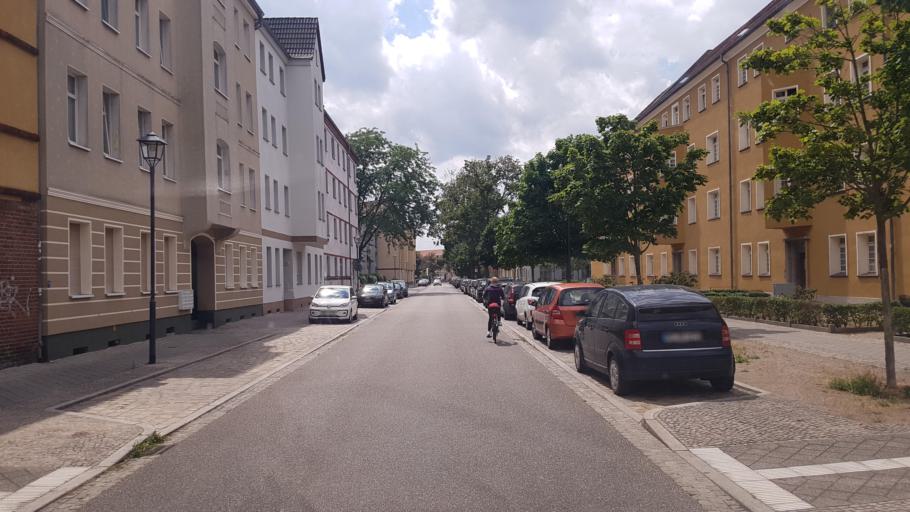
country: DE
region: Brandenburg
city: Brandenburg an der Havel
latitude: 52.4023
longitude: 12.5490
